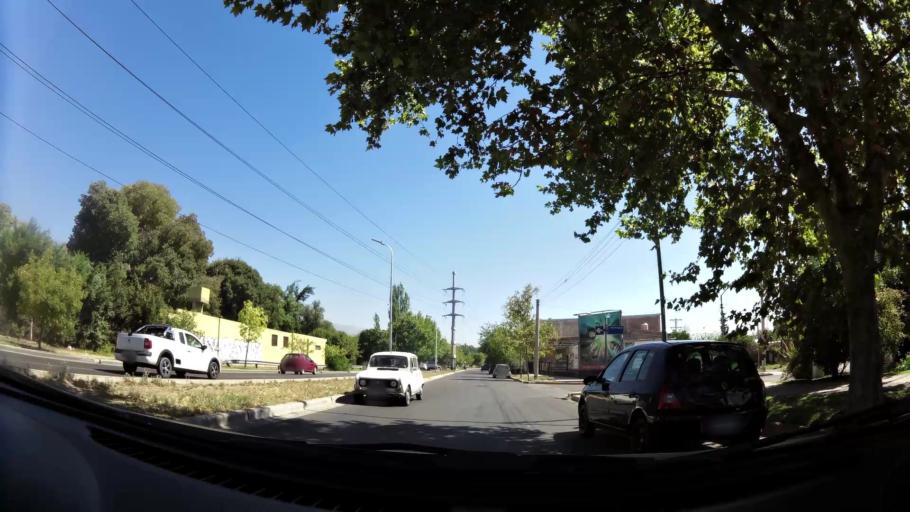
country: AR
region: Mendoza
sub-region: Departamento de Godoy Cruz
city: Godoy Cruz
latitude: -32.9081
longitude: -68.8646
